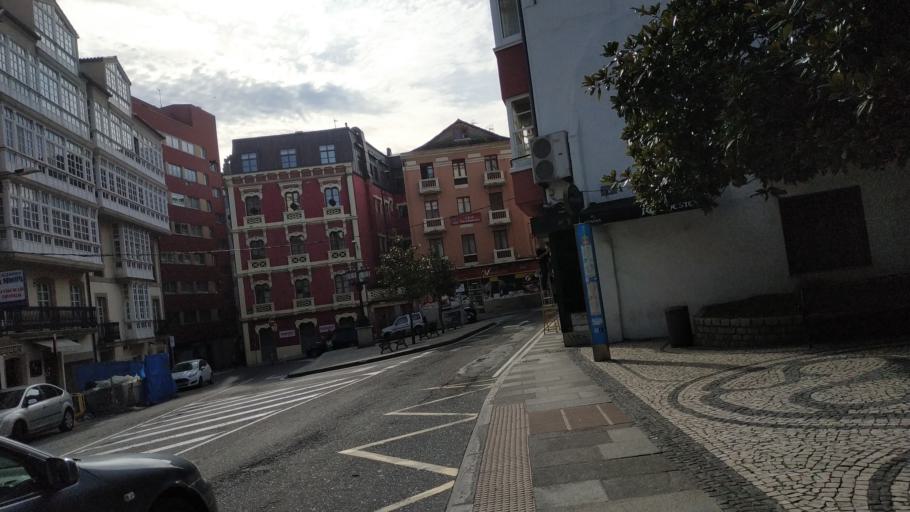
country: ES
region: Galicia
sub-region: Provincia da Coruna
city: A Coruna
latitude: 43.3726
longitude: -8.3992
